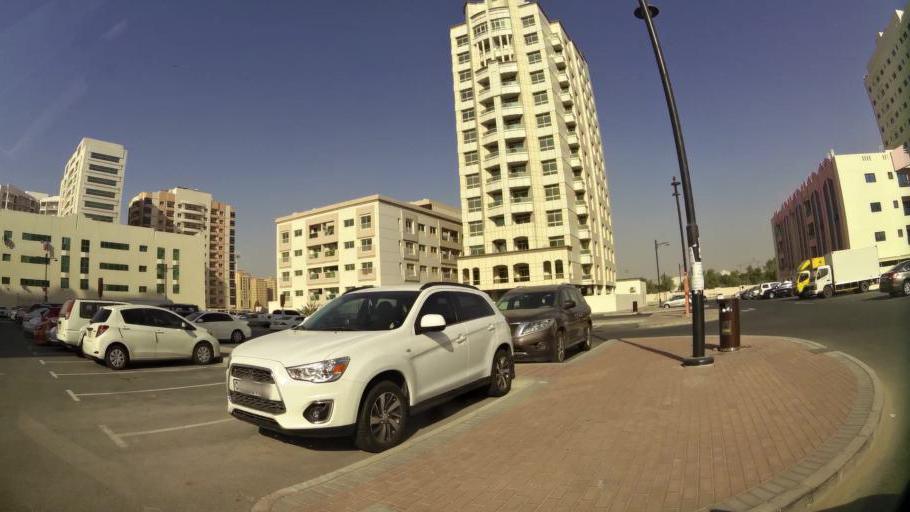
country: AE
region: Ash Shariqah
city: Sharjah
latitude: 25.2883
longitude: 55.3718
